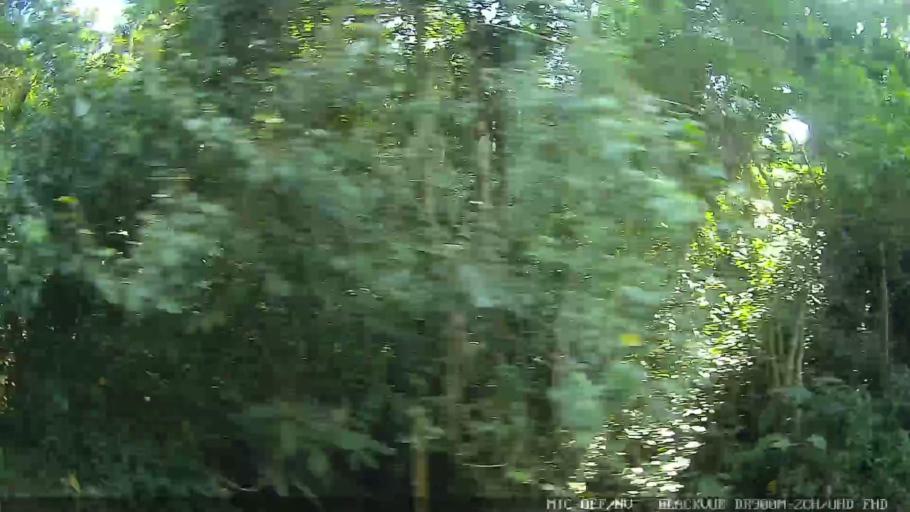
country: BR
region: Sao Paulo
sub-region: Guaruja
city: Guaruja
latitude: -24.0095
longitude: -46.3034
